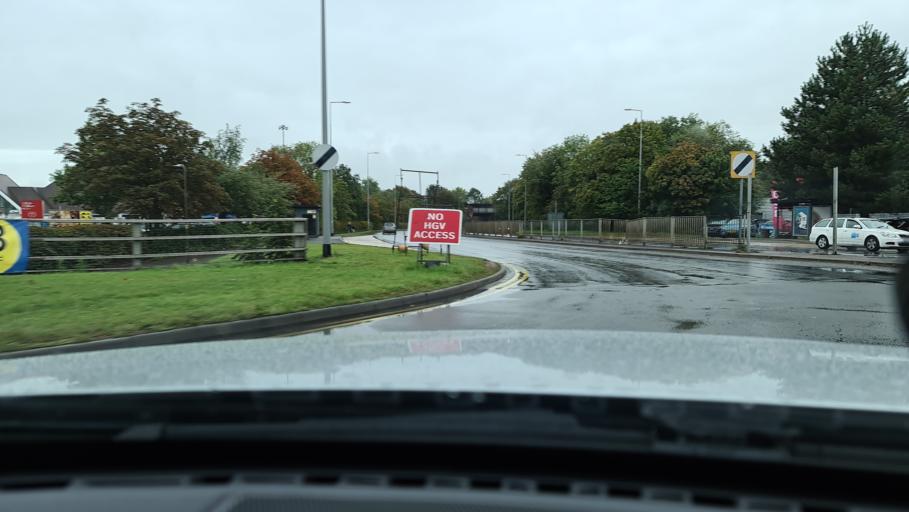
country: GB
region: England
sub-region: Buckinghamshire
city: Bletchley
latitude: 52.0025
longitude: -0.7260
